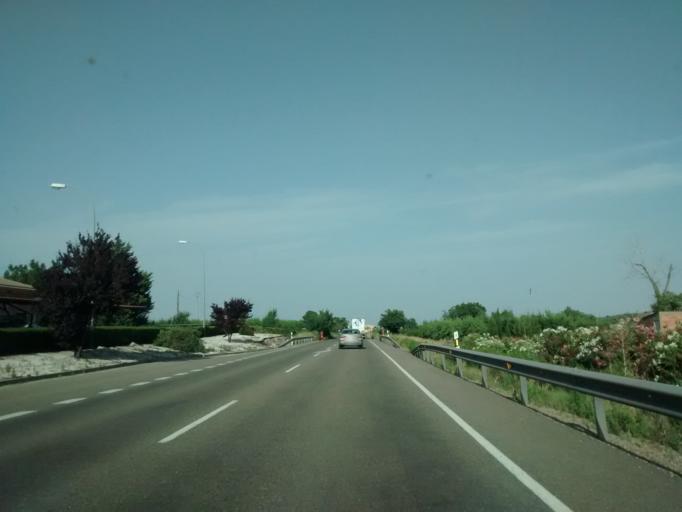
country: ES
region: Aragon
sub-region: Provincia de Zaragoza
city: Bulbuente
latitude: 41.8189
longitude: -1.6092
